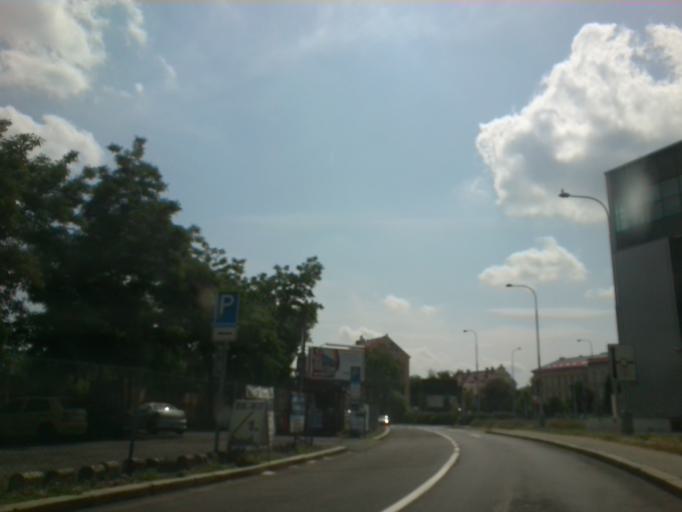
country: CZ
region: Praha
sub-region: Praha 8
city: Karlin
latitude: 50.1087
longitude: 14.4426
